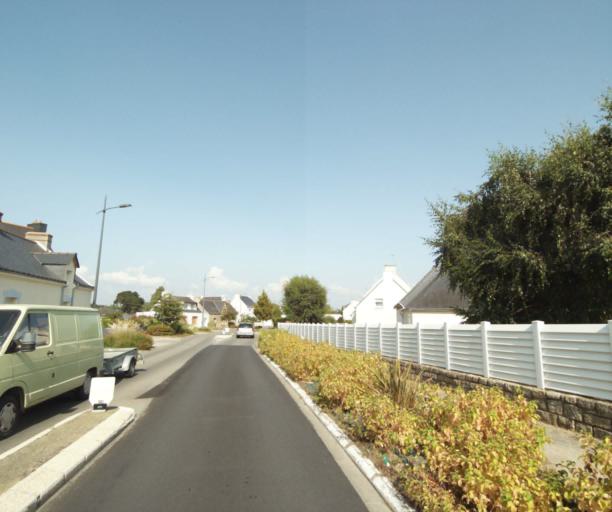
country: FR
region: Brittany
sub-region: Departement du Morbihan
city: Riantec
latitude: 47.7098
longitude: -3.3297
